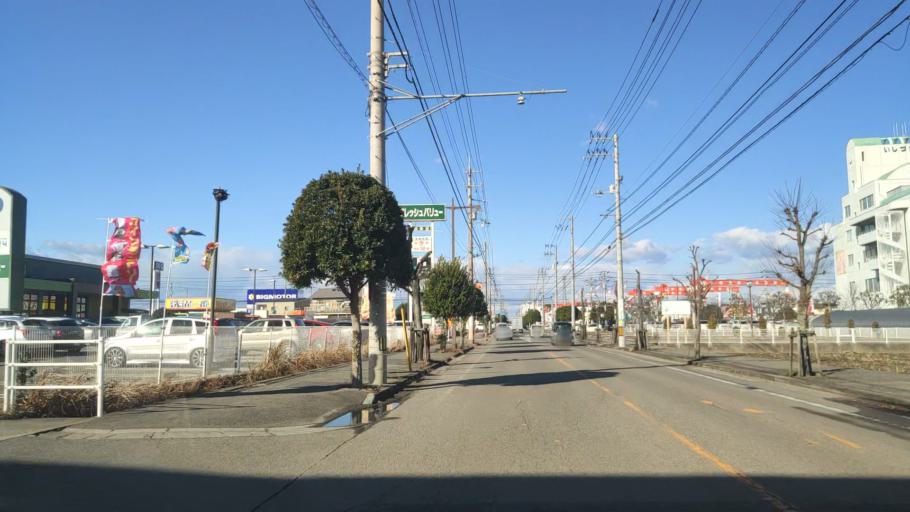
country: JP
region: Ehime
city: Saijo
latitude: 33.9279
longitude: 133.1905
